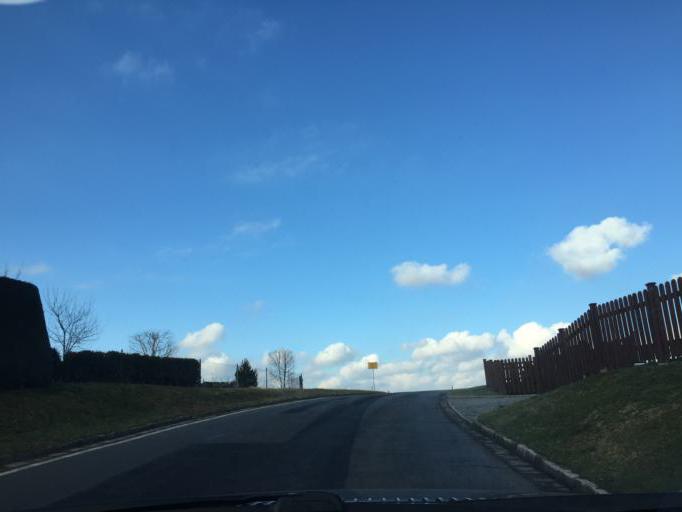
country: DE
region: Saxony
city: Tauscha
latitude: 51.2601
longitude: 13.7713
